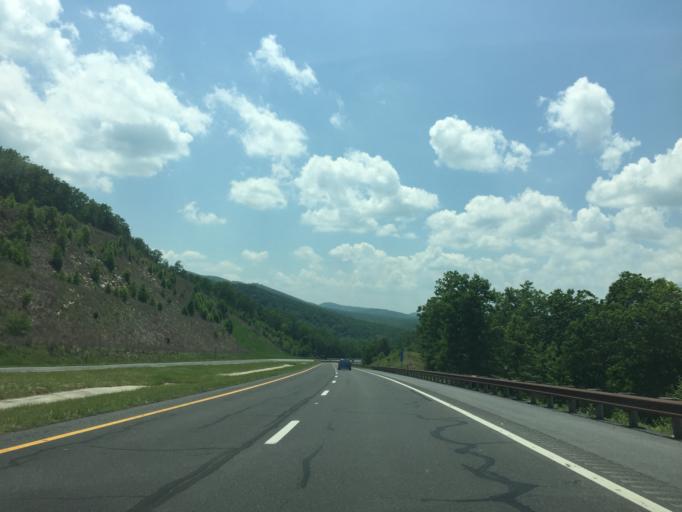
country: US
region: Virginia
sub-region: Shenandoah County
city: Woodstock
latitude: 39.0700
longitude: -78.6497
